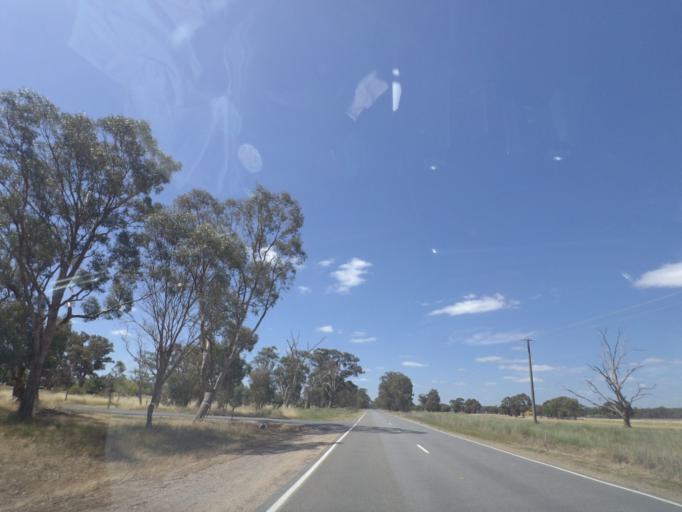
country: AU
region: Victoria
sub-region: Wangaratta
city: Wangaratta
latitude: -36.4169
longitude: 146.2643
